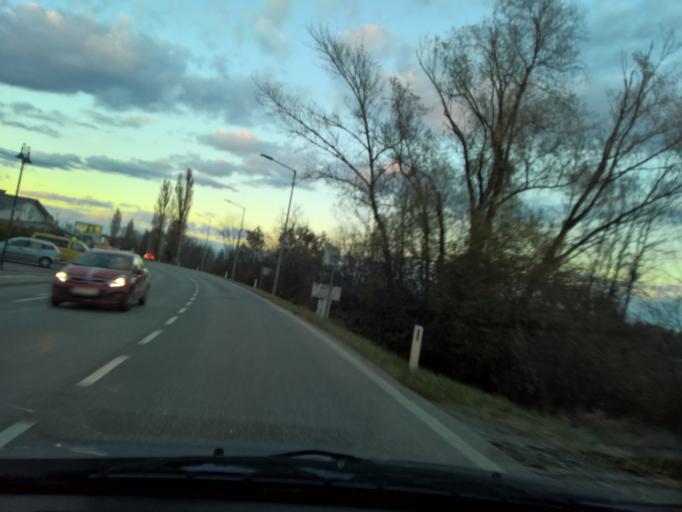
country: AT
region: Styria
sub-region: Politischer Bezirk Graz-Umgebung
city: Kalsdorf bei Graz
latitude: 46.9724
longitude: 15.4728
